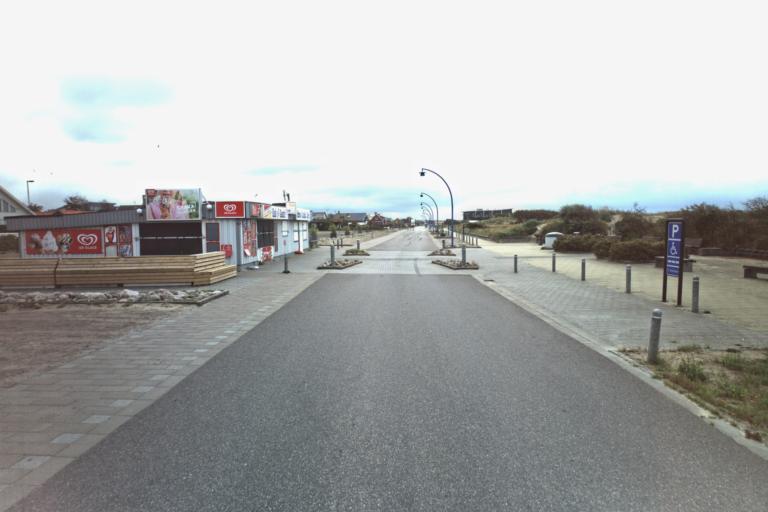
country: SE
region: Halland
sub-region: Falkenbergs Kommun
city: Falkenberg
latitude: 56.8866
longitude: 12.5010
